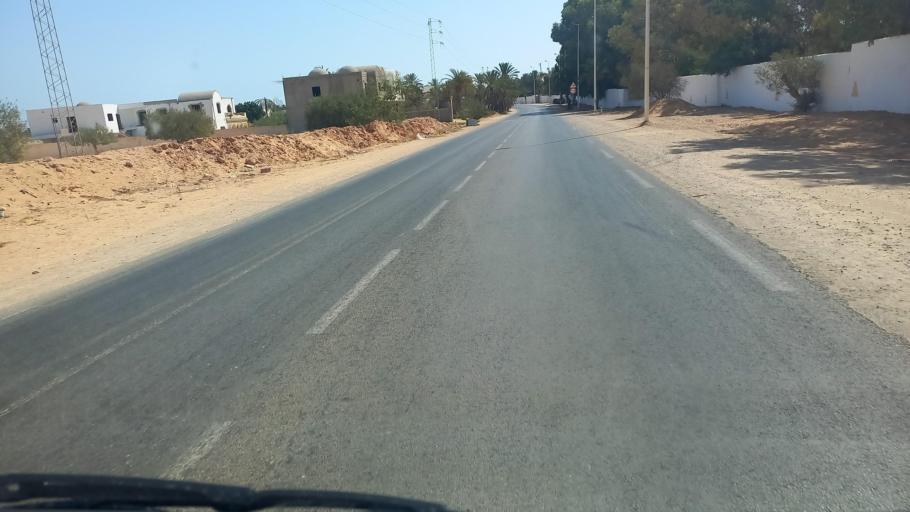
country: TN
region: Madanin
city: Midoun
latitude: 33.7808
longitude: 11.0444
